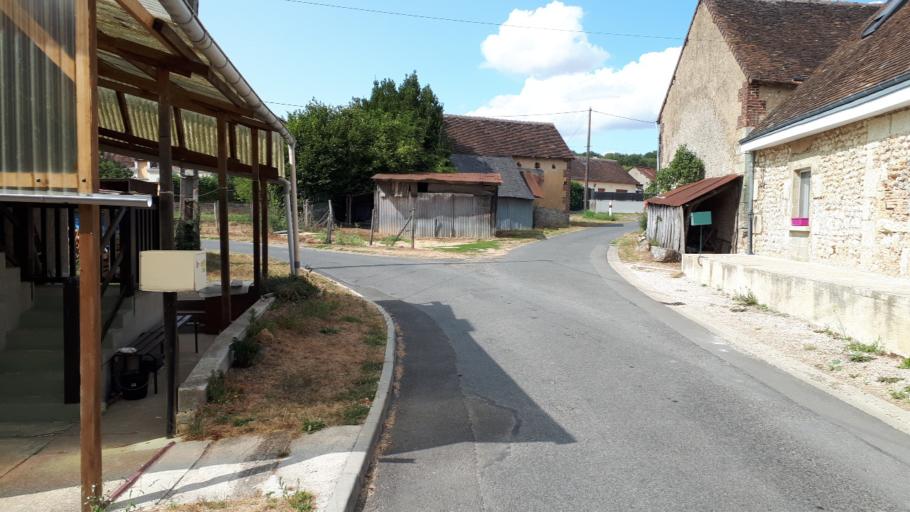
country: FR
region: Centre
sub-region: Departement du Loir-et-Cher
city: Aze
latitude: 47.8328
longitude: 0.9837
